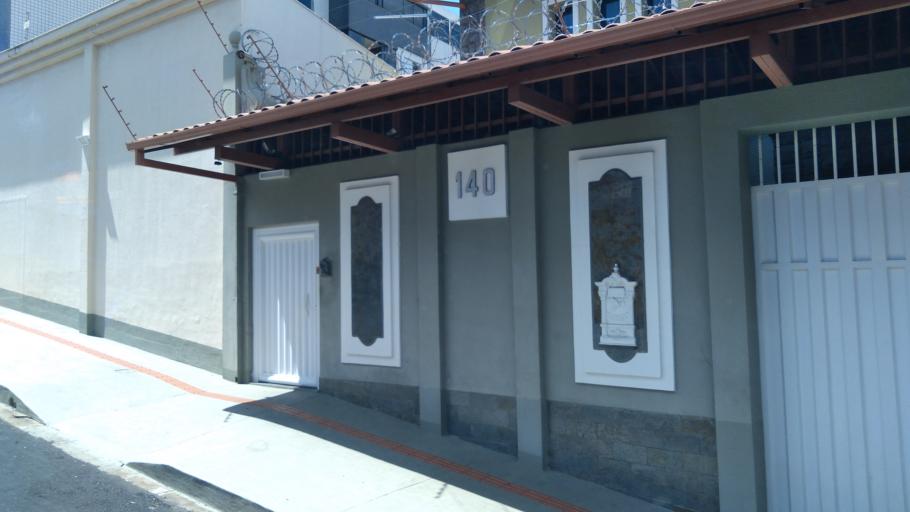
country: BR
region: Minas Gerais
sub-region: Belo Horizonte
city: Belo Horizonte
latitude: -19.8712
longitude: -43.9200
